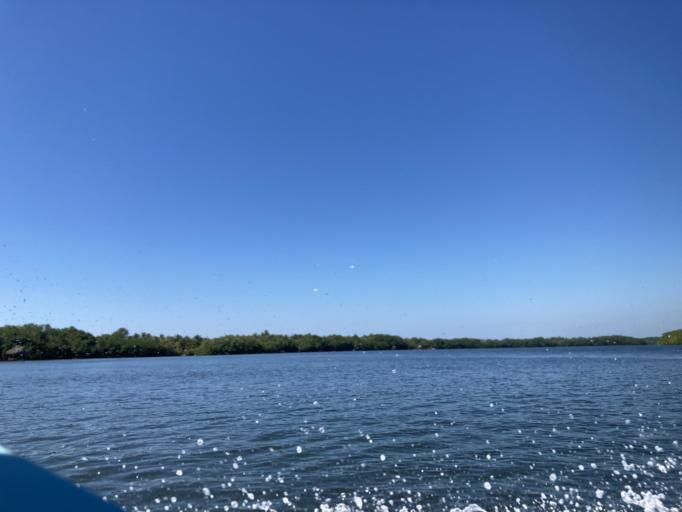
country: GT
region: Jutiapa
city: Pasaco
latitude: 13.8104
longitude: -90.2789
